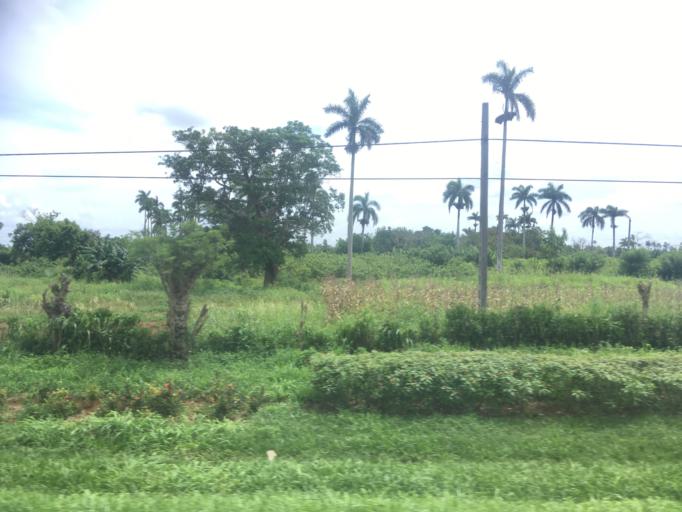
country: CU
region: Matanzas
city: Perico
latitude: 22.7759
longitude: -81.0325
